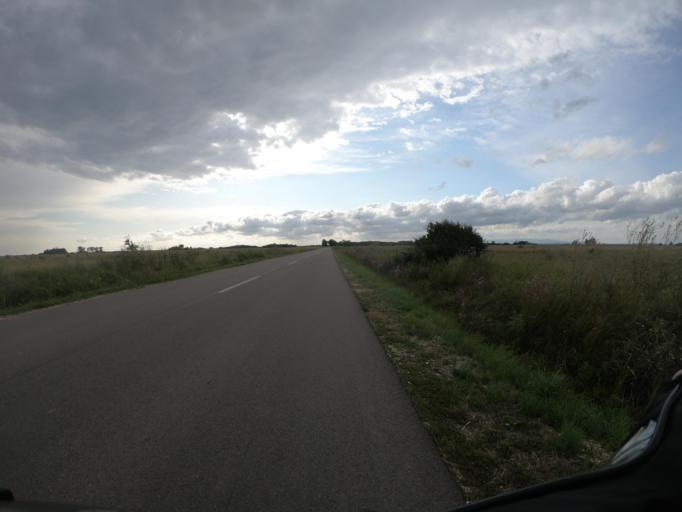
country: HU
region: Borsod-Abauj-Zemplen
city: Mezocsat
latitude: 47.8197
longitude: 20.8618
